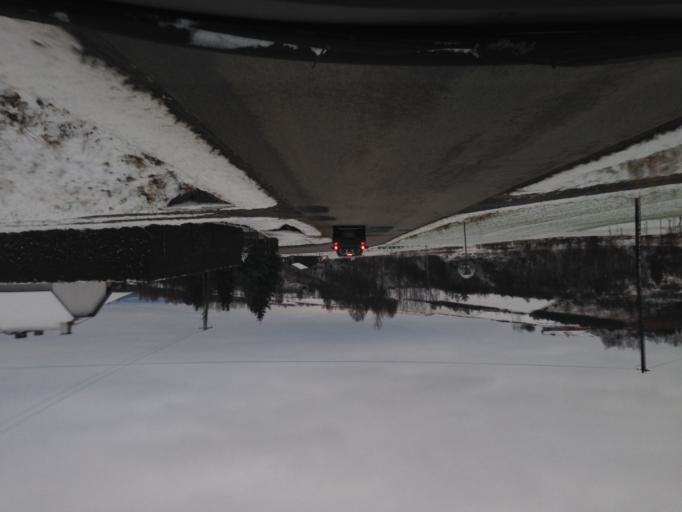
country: PL
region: Lesser Poland Voivodeship
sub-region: Powiat gorlicki
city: Moszczenica
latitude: 49.7471
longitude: 21.0831
